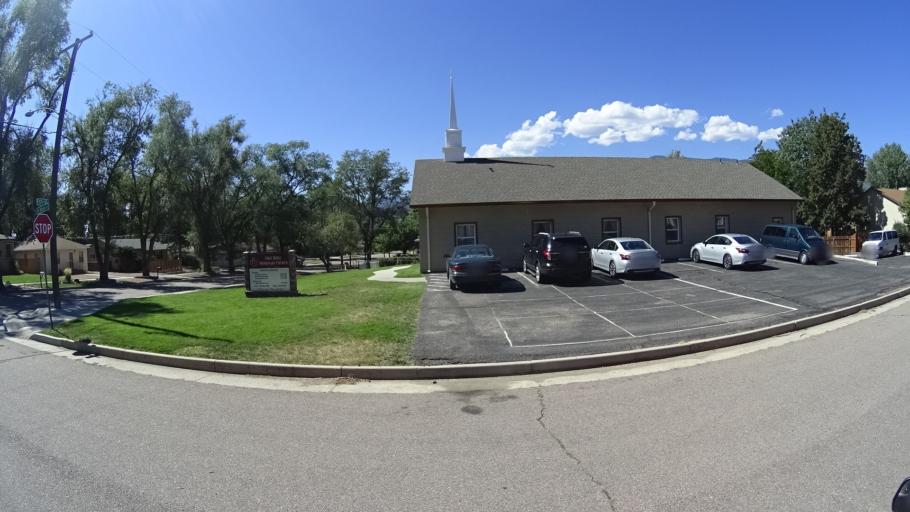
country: US
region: Colorado
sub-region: El Paso County
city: Colorado Springs
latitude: 38.8458
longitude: -104.8464
